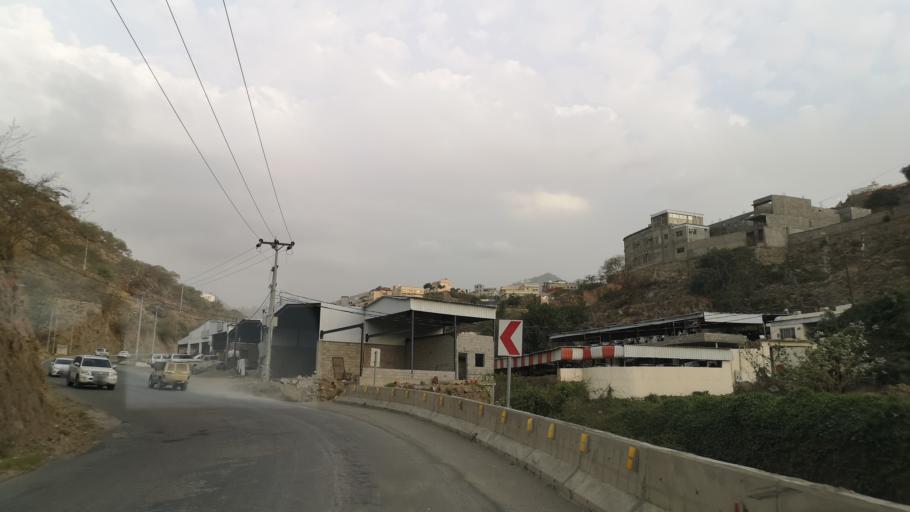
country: YE
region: Sa'dah
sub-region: Monabbih
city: Suq al Khamis
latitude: 17.3491
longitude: 43.1379
